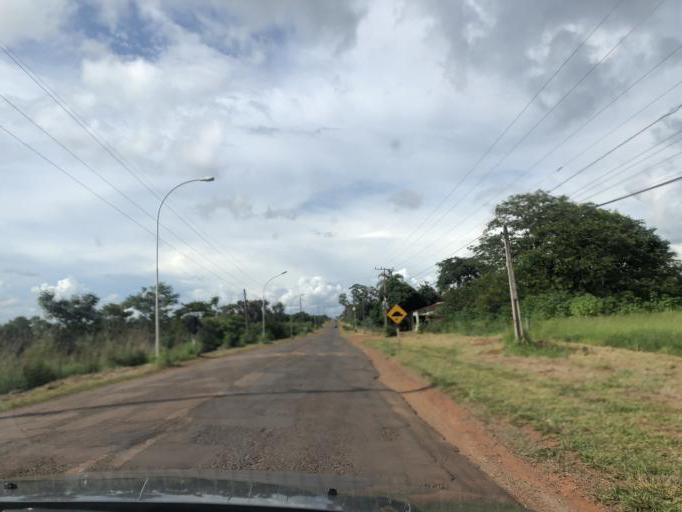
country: BR
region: Federal District
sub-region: Brasilia
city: Brasilia
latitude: -15.7441
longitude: -48.1257
